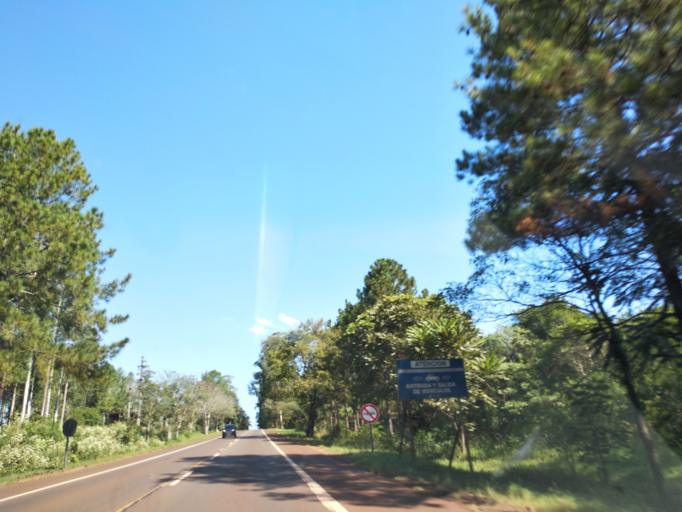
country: AR
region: Misiones
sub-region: Departamento de Montecarlo
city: Montecarlo
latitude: -26.5587
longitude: -54.7247
